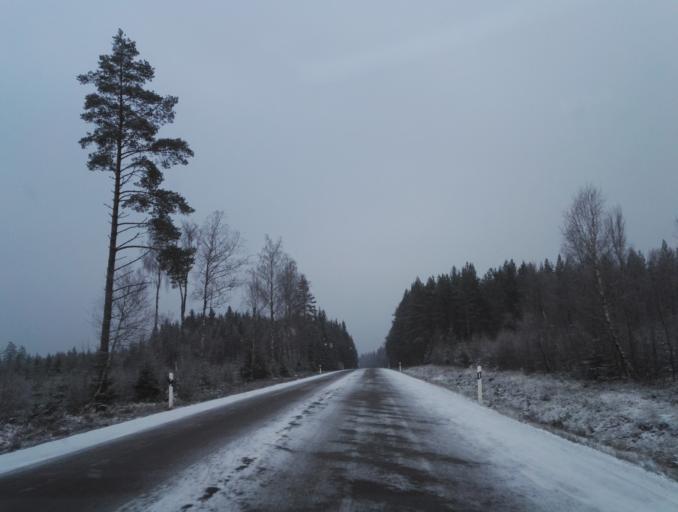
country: SE
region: Kronoberg
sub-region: Uppvidinge Kommun
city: Lenhovda
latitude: 56.8967
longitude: 15.3697
